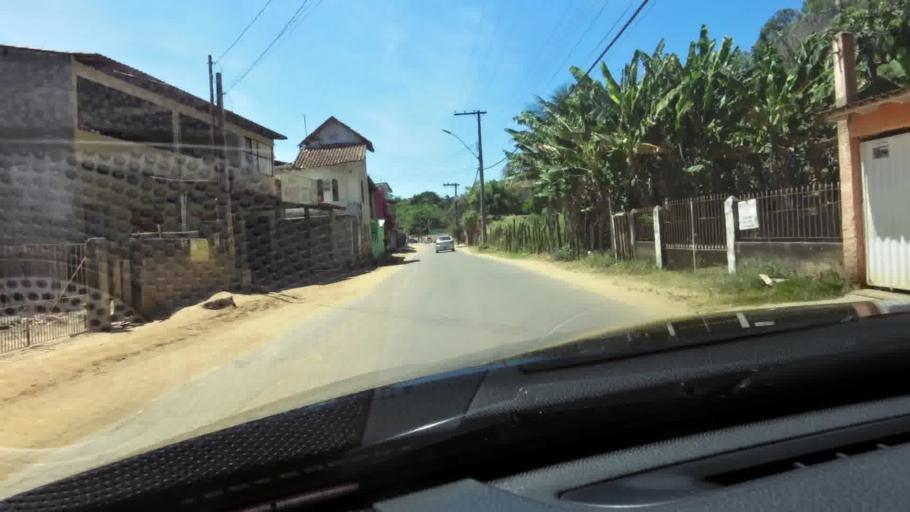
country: BR
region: Espirito Santo
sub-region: Guarapari
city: Guarapari
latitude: -20.6206
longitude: -40.4673
